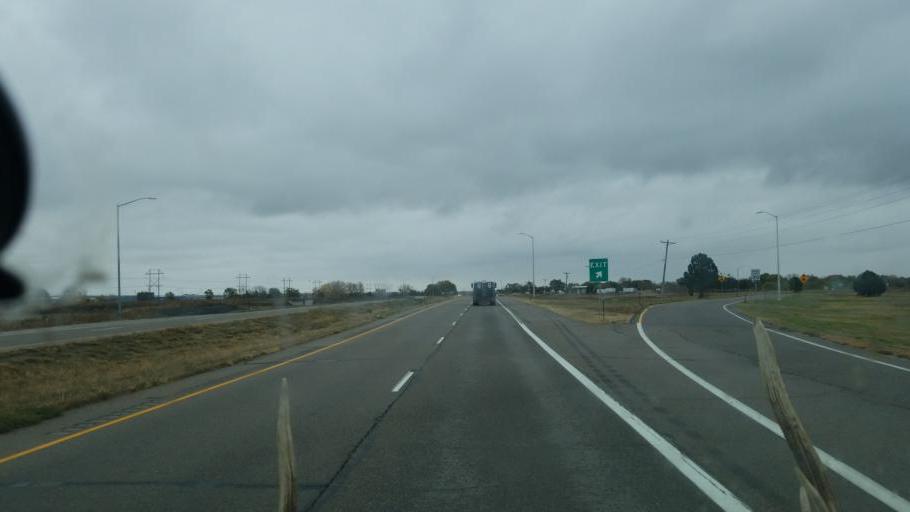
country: US
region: Colorado
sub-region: Pueblo County
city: Pueblo
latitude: 38.2747
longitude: -104.5097
